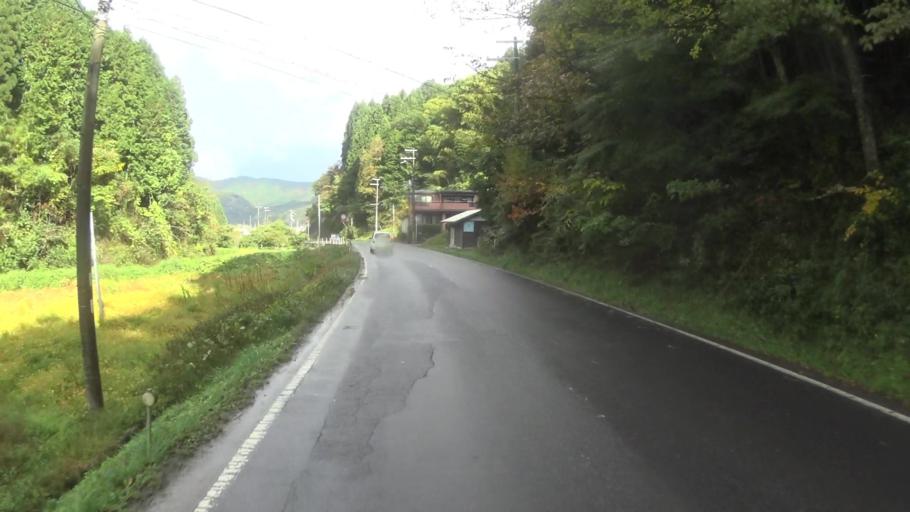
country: JP
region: Kyoto
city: Fukuchiyama
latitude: 35.3821
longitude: 135.1792
